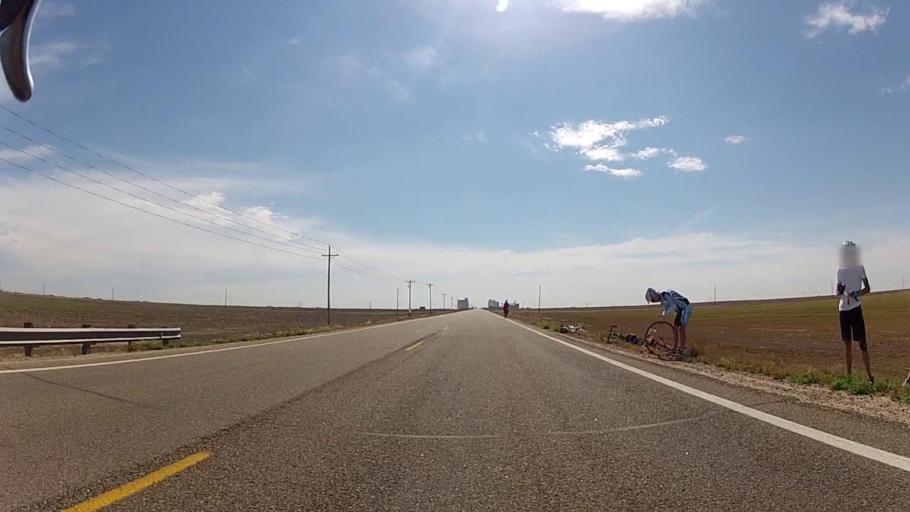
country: US
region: Kansas
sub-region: Grant County
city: Ulysses
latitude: 37.5618
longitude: -101.2568
